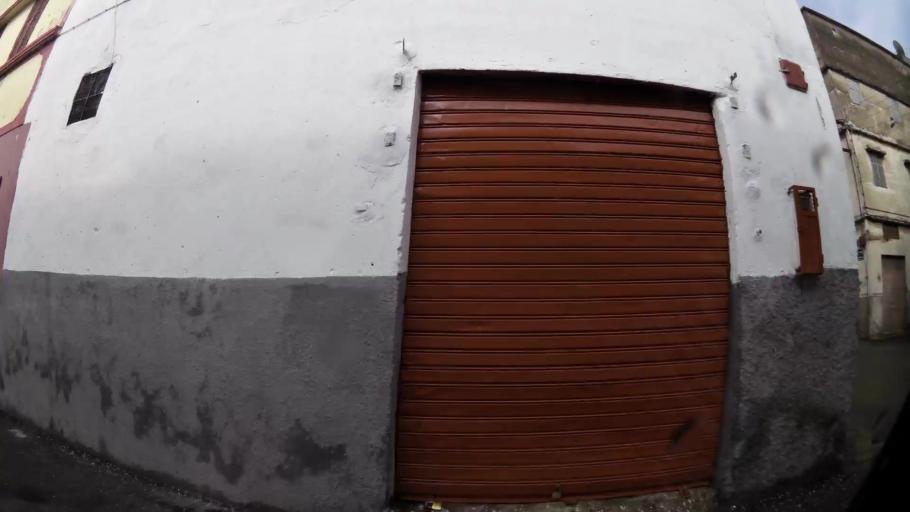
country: MA
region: Grand Casablanca
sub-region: Casablanca
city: Casablanca
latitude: 33.5484
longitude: -7.5709
